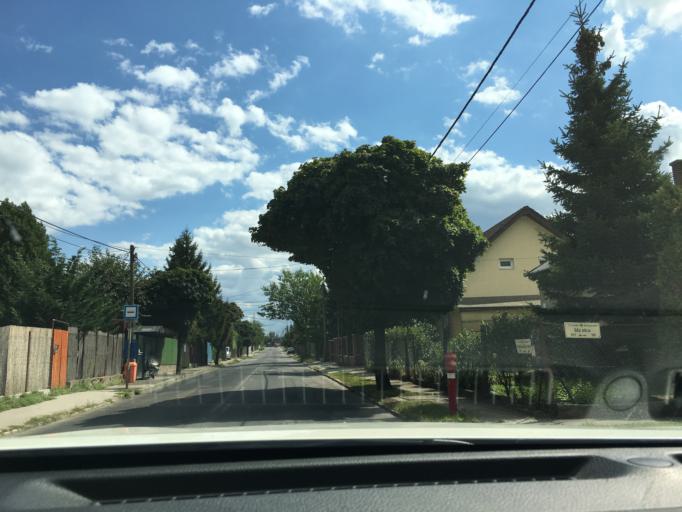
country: HU
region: Budapest
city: Budapest XVI. keruelet
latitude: 47.5263
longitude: 19.1821
